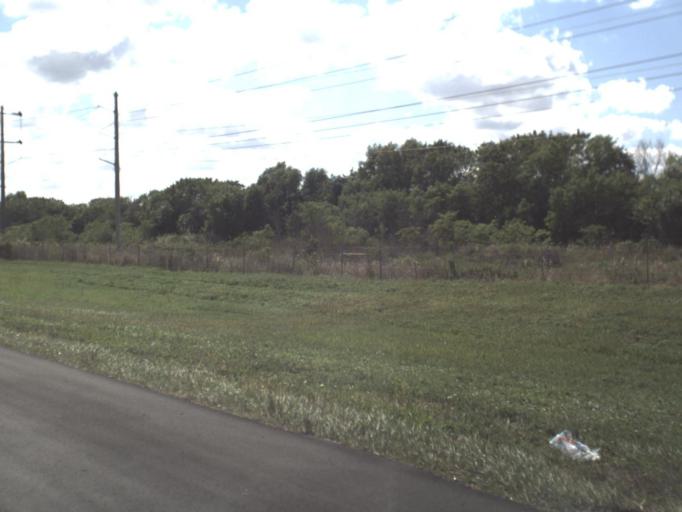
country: US
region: Florida
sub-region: Broward County
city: Tamarac
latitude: 26.2228
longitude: -80.2967
